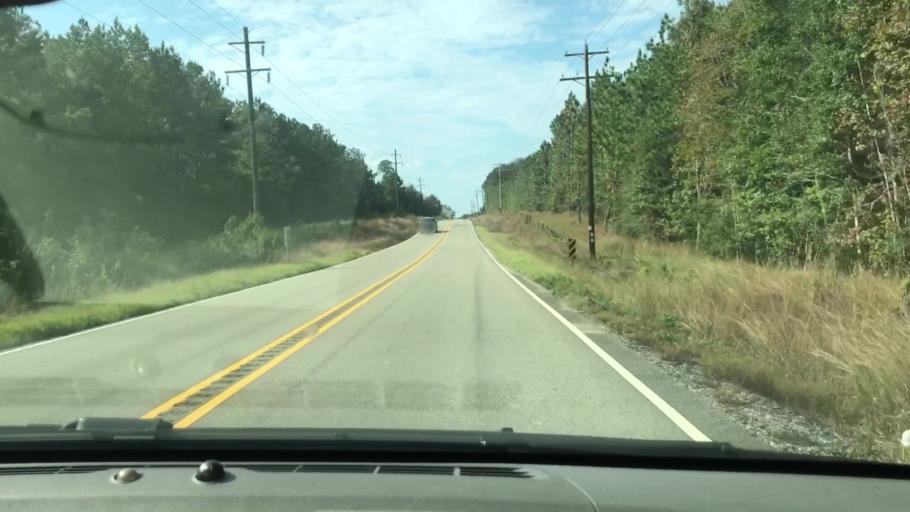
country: US
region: Louisiana
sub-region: Saint Tammany Parish
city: Abita Springs
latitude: 30.5283
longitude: -89.9170
